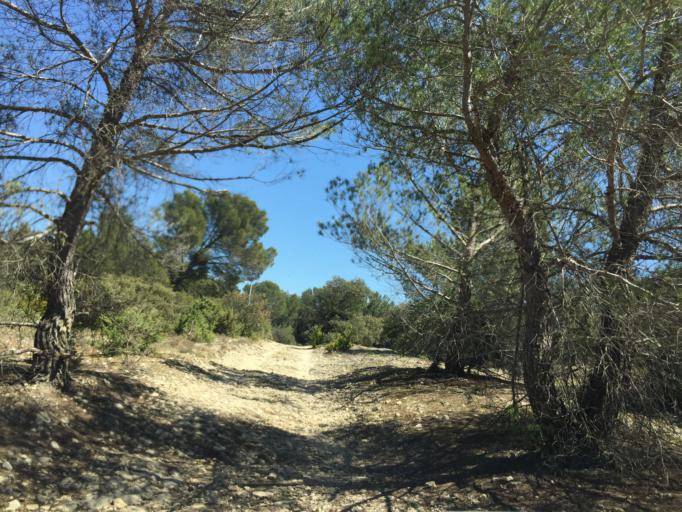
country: FR
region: Languedoc-Roussillon
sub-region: Departement du Gard
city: Roquemaure
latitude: 44.0526
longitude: 4.8037
